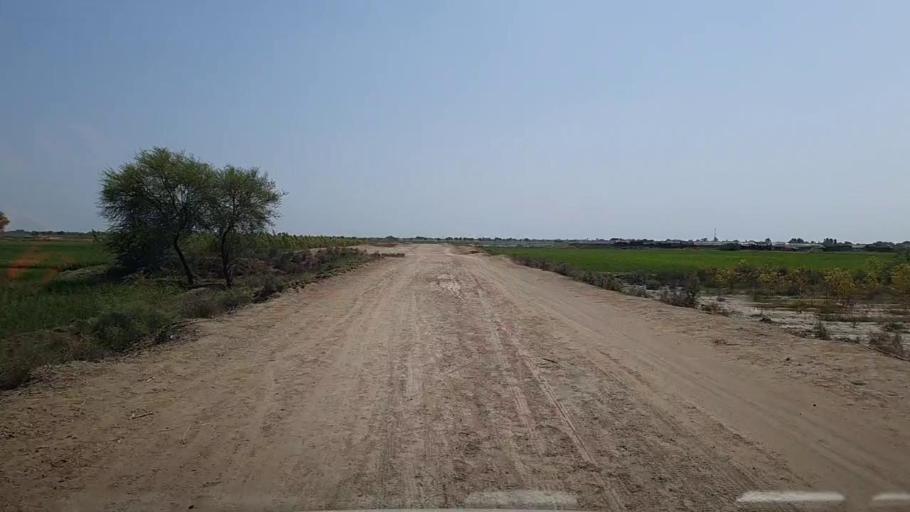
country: PK
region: Sindh
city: Kario
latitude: 24.8292
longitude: 68.7126
